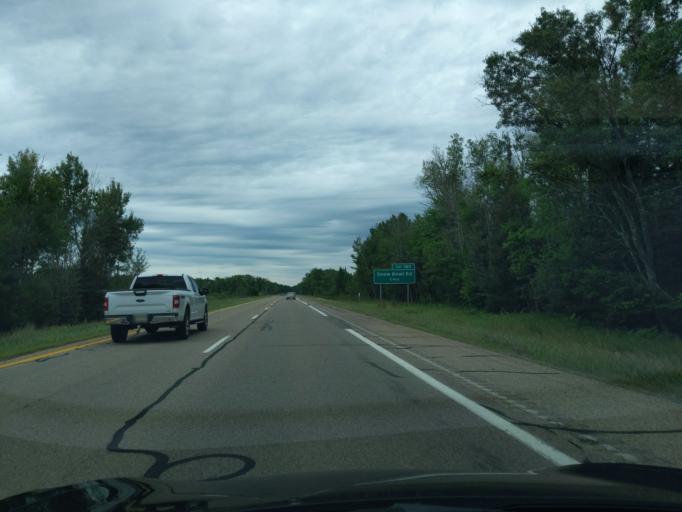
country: US
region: Michigan
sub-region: Roscommon County
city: Houghton Lake
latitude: 44.2892
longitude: -84.8009
